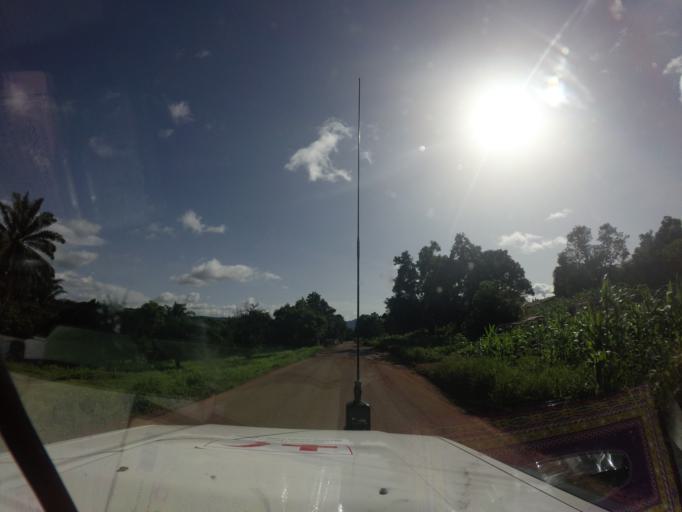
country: GN
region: Mamou
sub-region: Mamou Prefecture
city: Mamou
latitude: 10.2820
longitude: -12.4317
